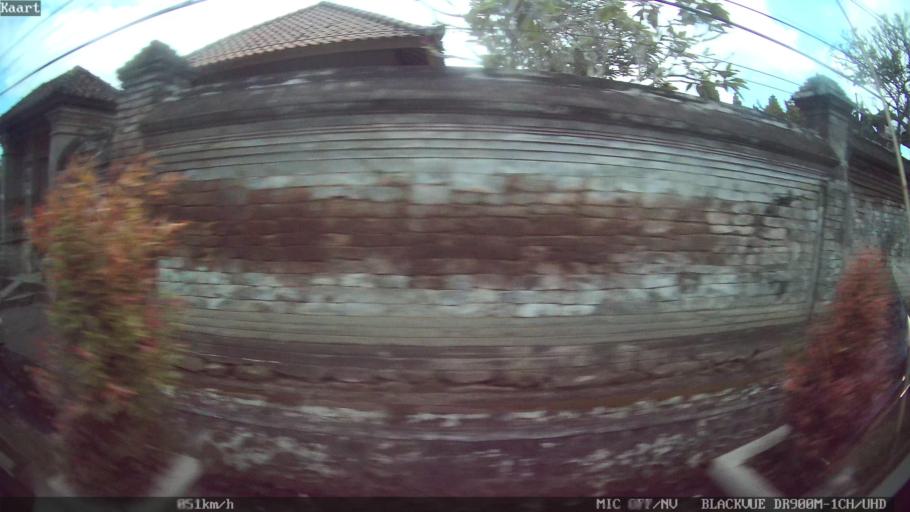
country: ID
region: Bali
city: Banjar Sedang
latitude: -8.5582
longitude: 115.2868
